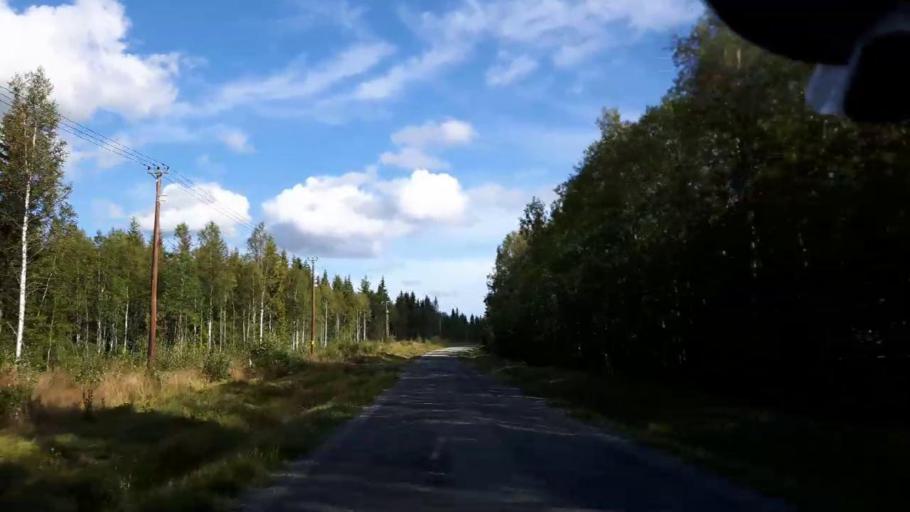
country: SE
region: Jaemtland
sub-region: Ragunda Kommun
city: Hammarstrand
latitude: 63.4419
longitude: 15.9809
